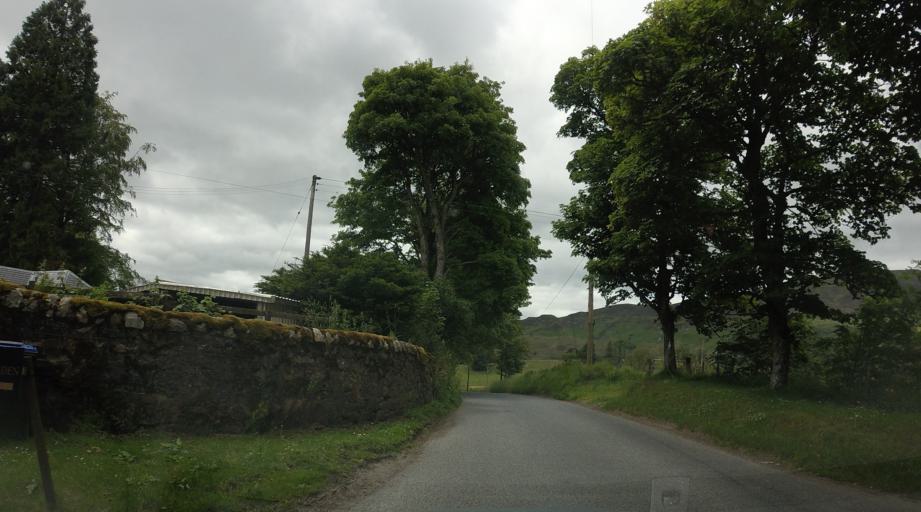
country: GB
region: Scotland
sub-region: Perth and Kinross
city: Aberfeldy
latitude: 56.7086
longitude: -4.1057
